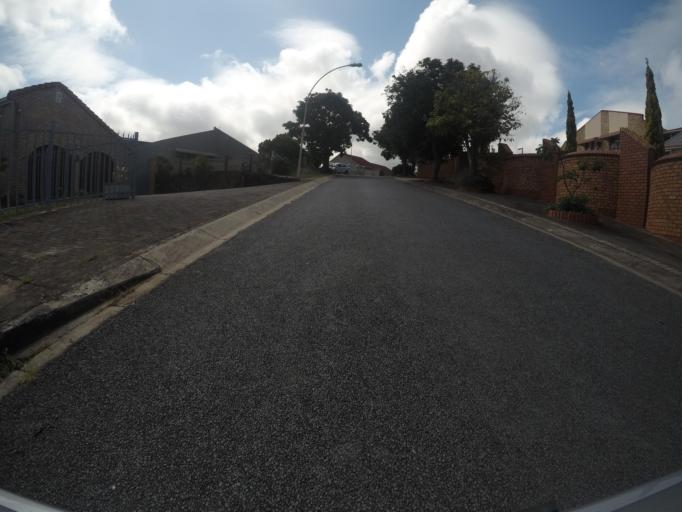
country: ZA
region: Eastern Cape
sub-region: Buffalo City Metropolitan Municipality
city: East London
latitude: -32.9983
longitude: 27.8865
